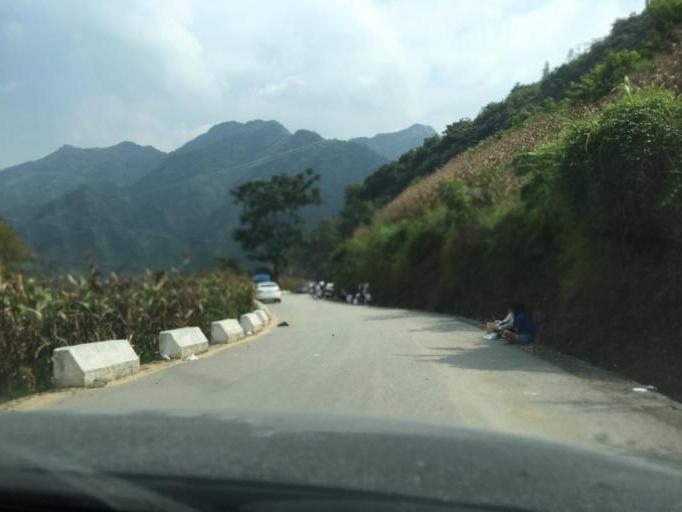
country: CN
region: Guangxi Zhuangzu Zizhiqu
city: Tongle
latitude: 25.2993
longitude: 106.2695
